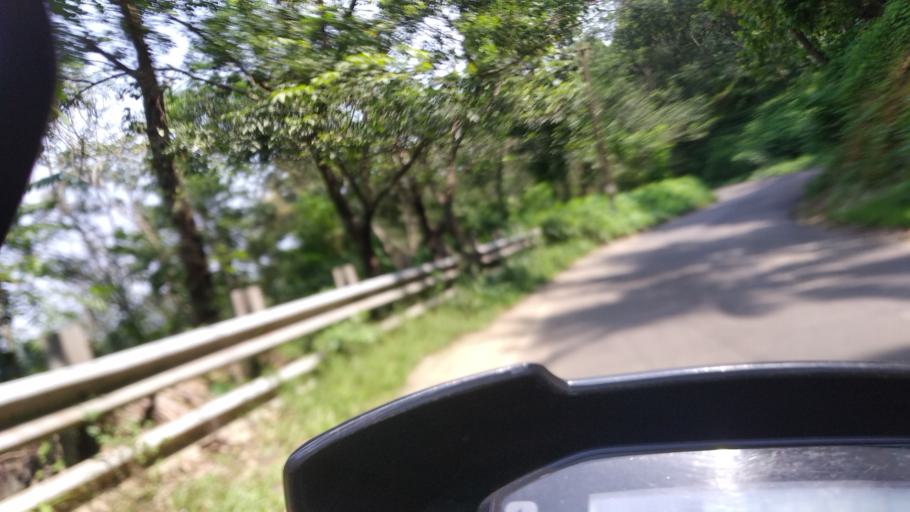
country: IN
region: Kerala
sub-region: Kottayam
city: Erattupetta
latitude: 9.6935
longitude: 76.8709
